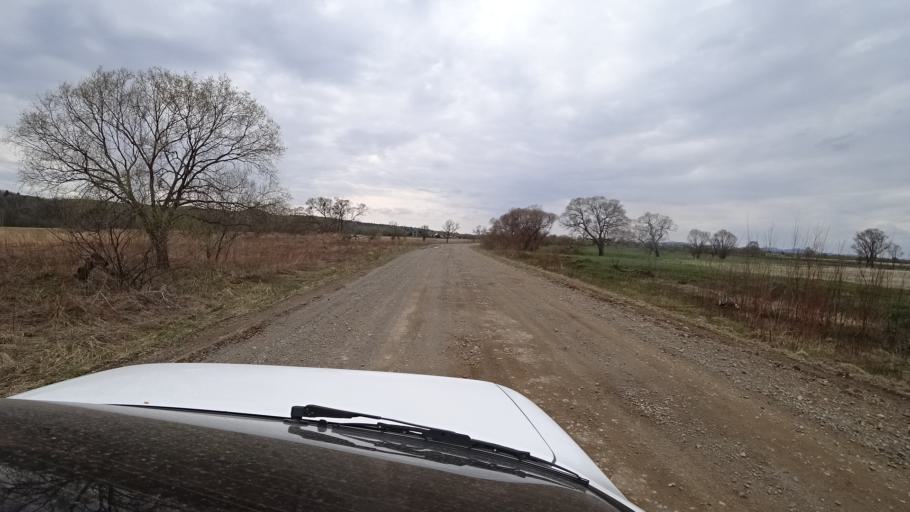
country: RU
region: Primorskiy
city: Novopokrovka
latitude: 45.4899
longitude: 134.4590
